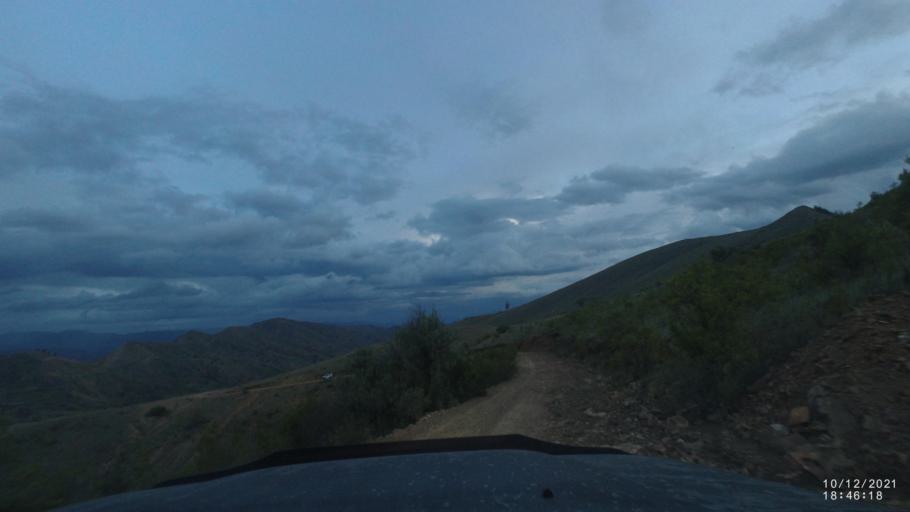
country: BO
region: Cochabamba
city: Tarata
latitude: -17.8777
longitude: -65.9766
